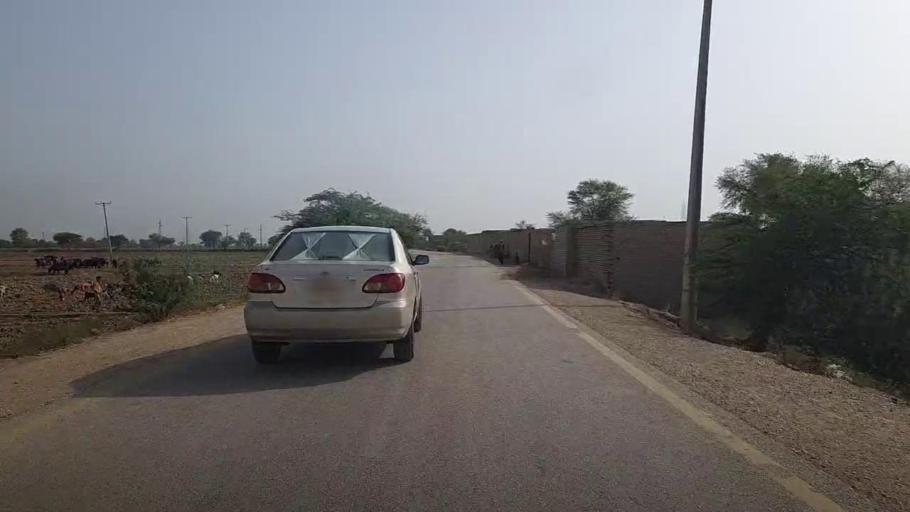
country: PK
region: Sindh
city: Khairpur Nathan Shah
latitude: 27.1017
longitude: 67.7562
